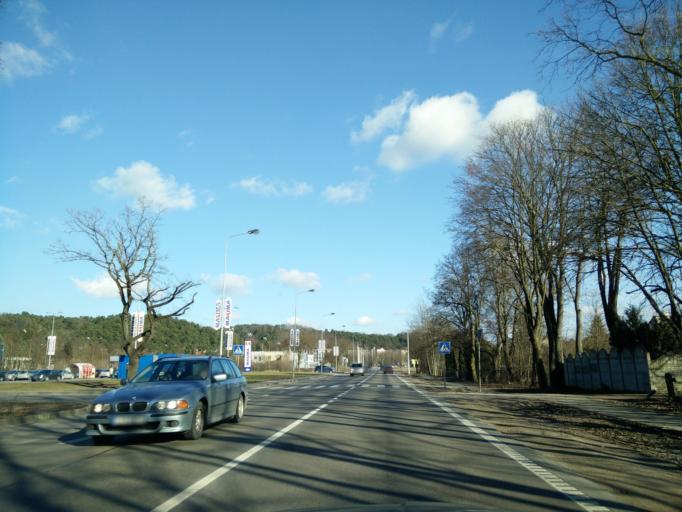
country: LT
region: Kauno apskritis
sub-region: Kauno rajonas
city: Akademija (Kaunas)
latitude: 54.9205
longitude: 23.8195
